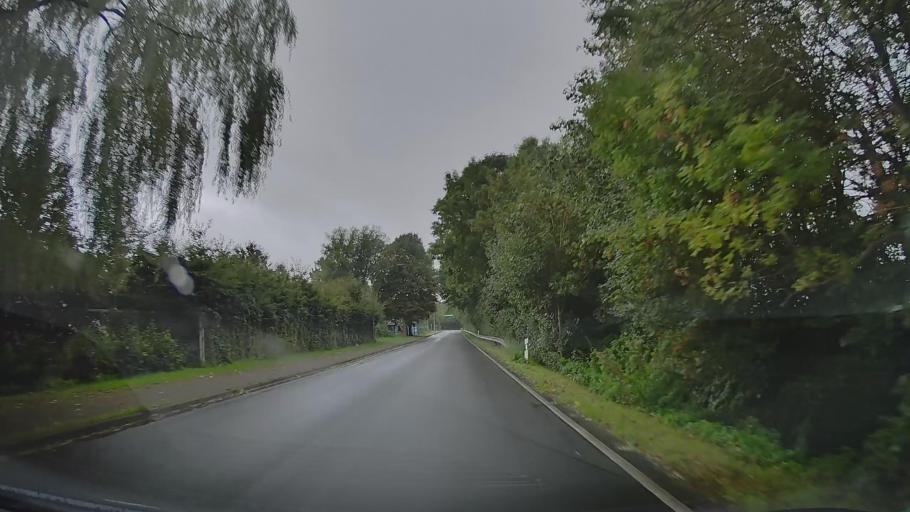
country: DE
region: Schleswig-Holstein
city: Buttel
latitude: 53.8989
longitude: 9.2222
